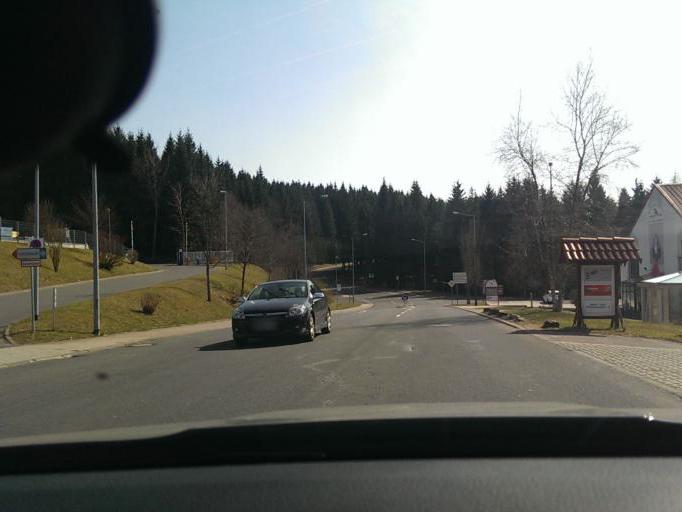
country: DE
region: Thuringia
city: Suhl
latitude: 50.5857
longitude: 10.7121
